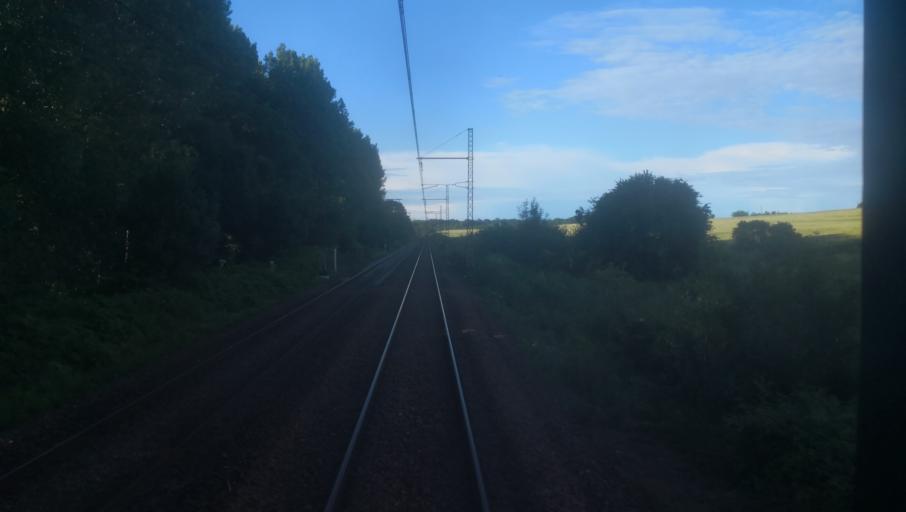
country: FR
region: Centre
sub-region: Departement de l'Indre
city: Reuilly
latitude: 47.0535
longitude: 2.0367
